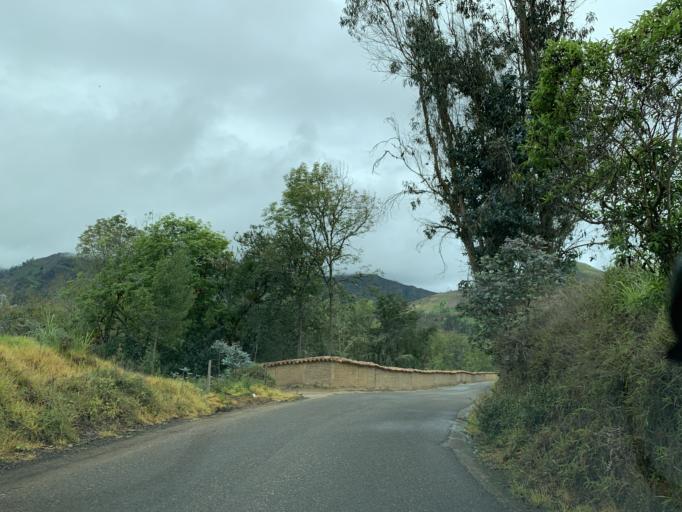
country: CO
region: Boyaca
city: Tibana
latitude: 5.3108
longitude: -73.4167
